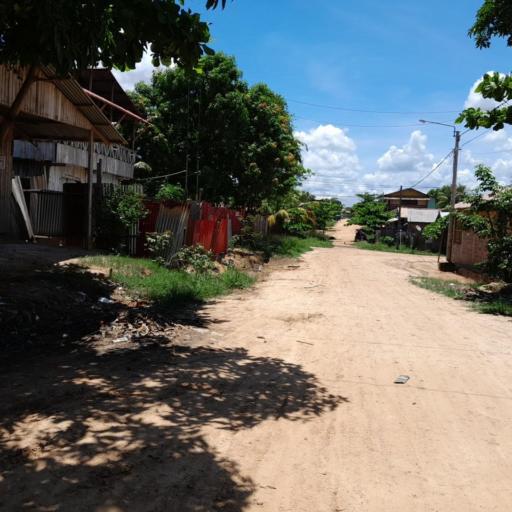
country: PE
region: Ucayali
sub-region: Provincia de Coronel Portillo
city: Puerto Callao
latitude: -8.3598
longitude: -74.5897
